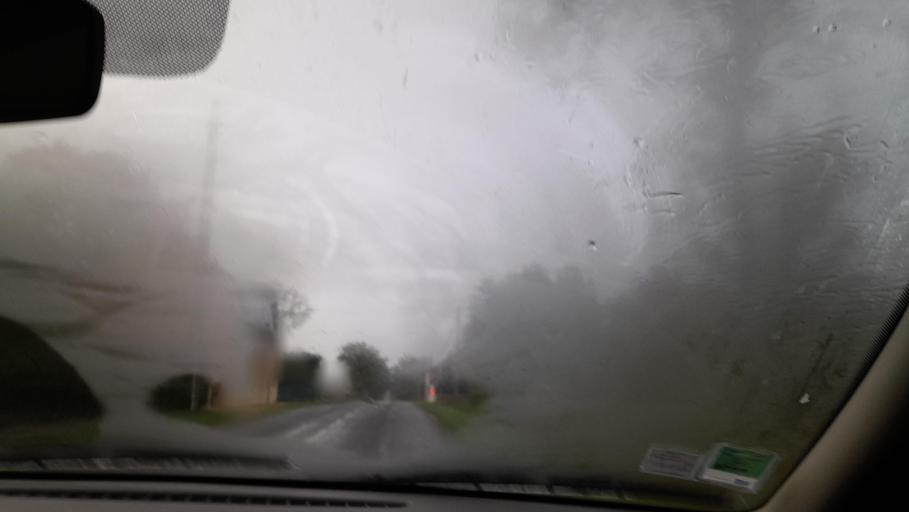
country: FR
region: Pays de la Loire
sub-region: Departement de la Mayenne
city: Ballots
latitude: 47.8595
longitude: -1.0507
